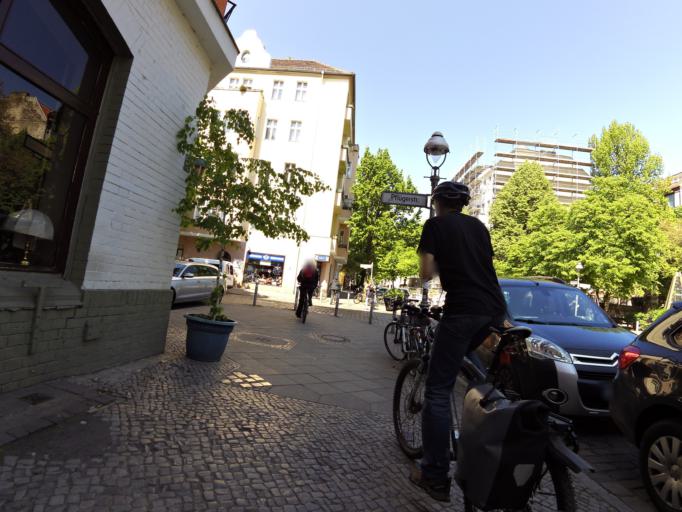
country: DE
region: Berlin
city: Berlin Treptow
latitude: 52.4912
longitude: 13.4261
